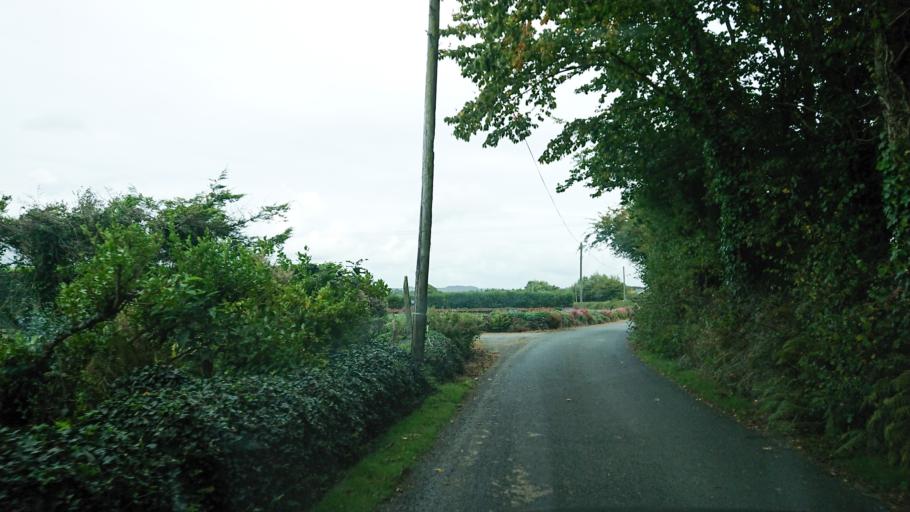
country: IE
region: Munster
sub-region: Waterford
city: Waterford
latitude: 52.2158
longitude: -7.0421
